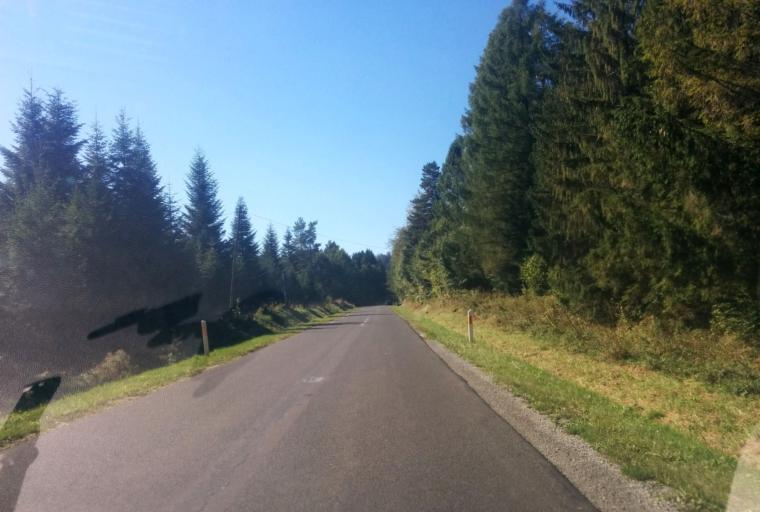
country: PL
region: Subcarpathian Voivodeship
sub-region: Powiat bieszczadzki
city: Czarna
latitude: 49.3140
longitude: 22.6463
